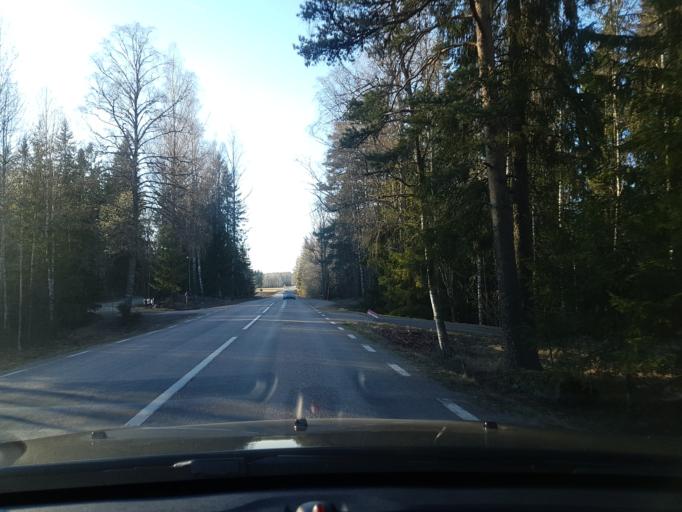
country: SE
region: Vaestmanland
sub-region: Sala Kommun
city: Sala
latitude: 59.9743
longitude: 16.4978
